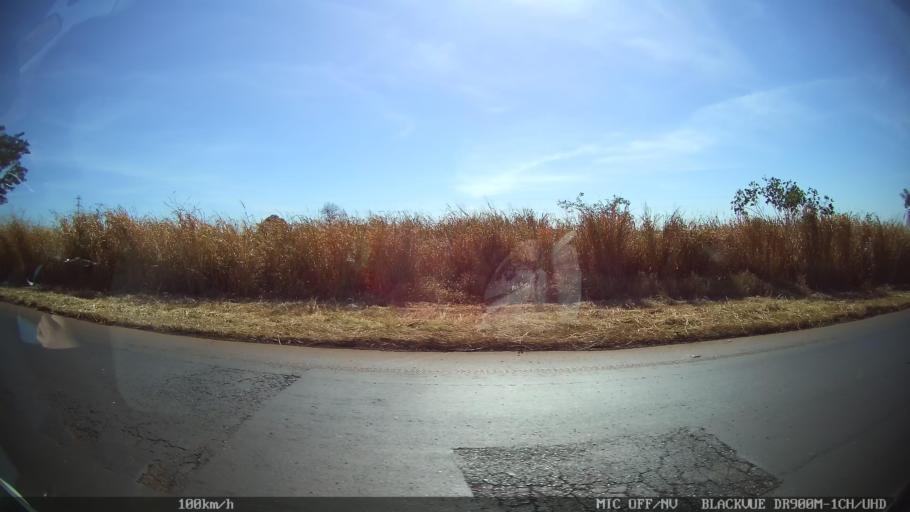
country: BR
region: Sao Paulo
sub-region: Barretos
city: Barretos
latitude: -20.4873
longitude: -48.5160
